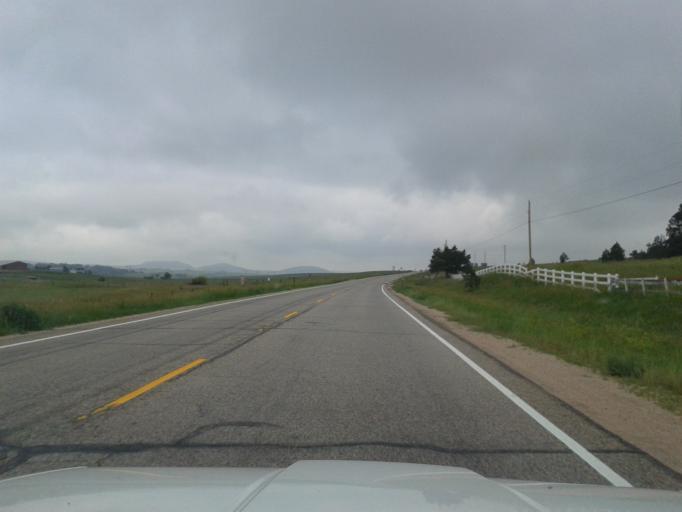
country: US
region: Colorado
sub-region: El Paso County
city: Gleneagle
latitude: 39.0916
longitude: -104.7708
